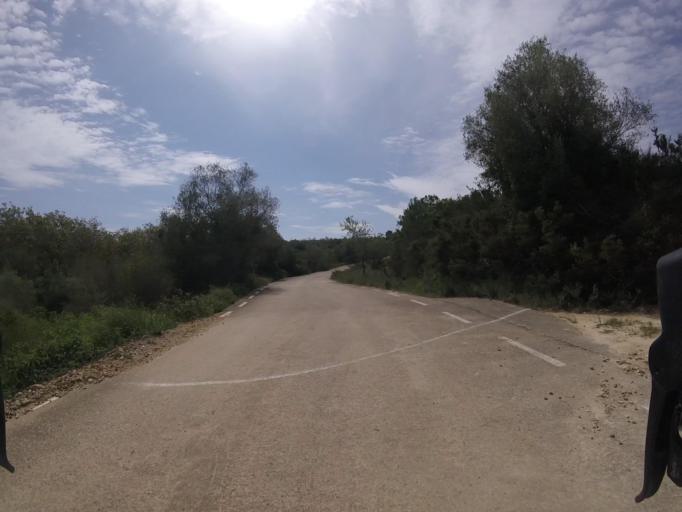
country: ES
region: Valencia
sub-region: Provincia de Castello
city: Cuevas de Vinroma
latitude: 40.2563
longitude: 0.1057
